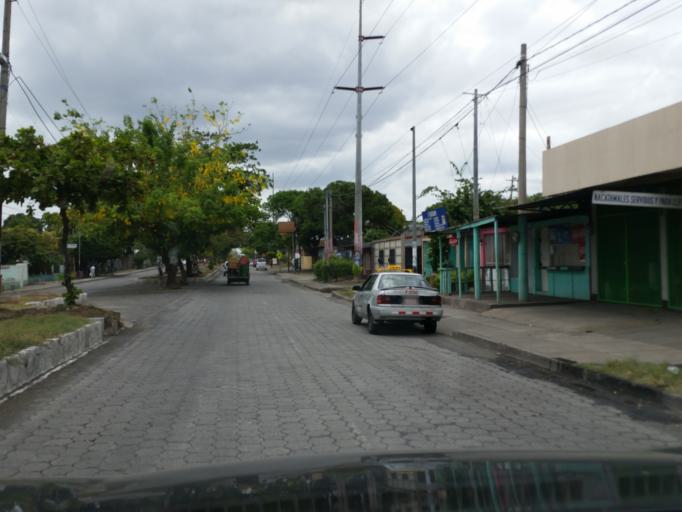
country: NI
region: Managua
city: Managua
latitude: 12.1275
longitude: -86.2369
